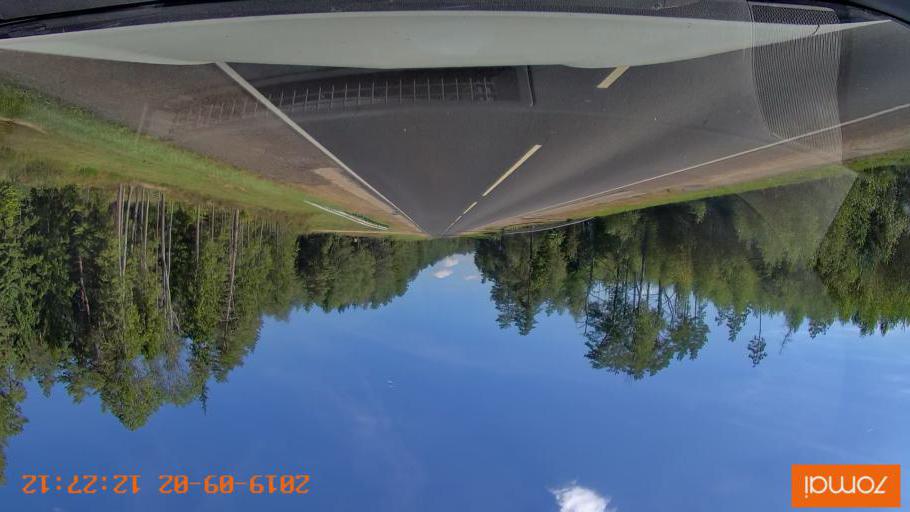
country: RU
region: Smolensk
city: Shumyachi
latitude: 53.8543
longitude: 32.5503
